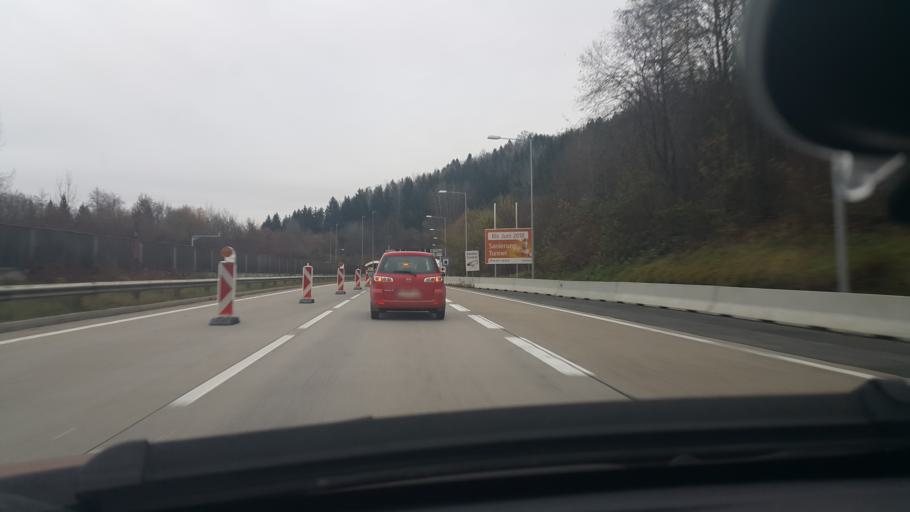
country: AT
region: Carinthia
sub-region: Klagenfurt am Woerthersee
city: Klagenfurt am Woerthersee
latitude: 46.6340
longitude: 14.2443
